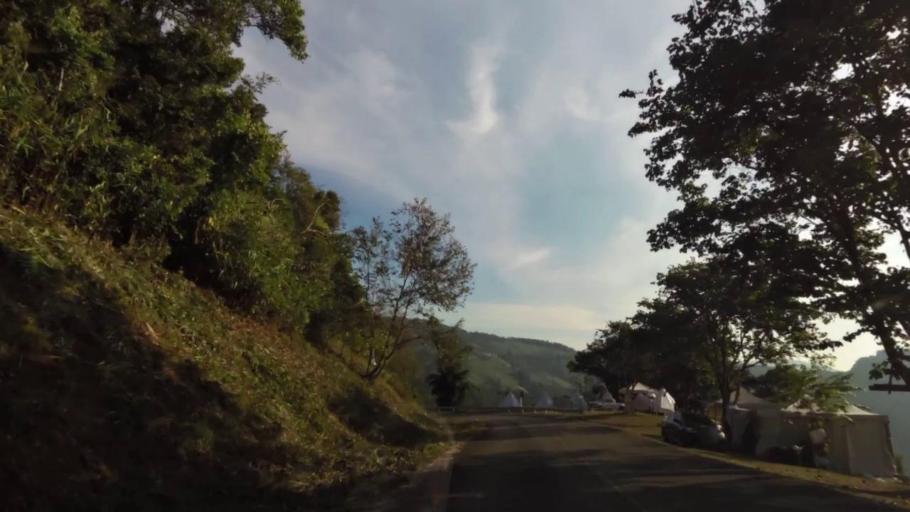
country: TH
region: Chiang Rai
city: Khun Tan
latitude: 19.8562
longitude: 100.4338
